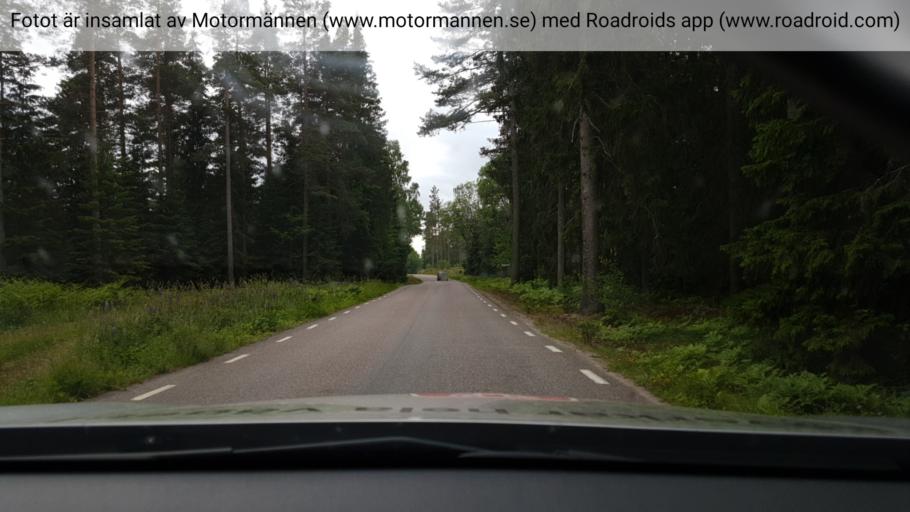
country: SE
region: Joenkoeping
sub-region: Habo Kommun
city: Habo
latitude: 58.0228
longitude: 14.0115
